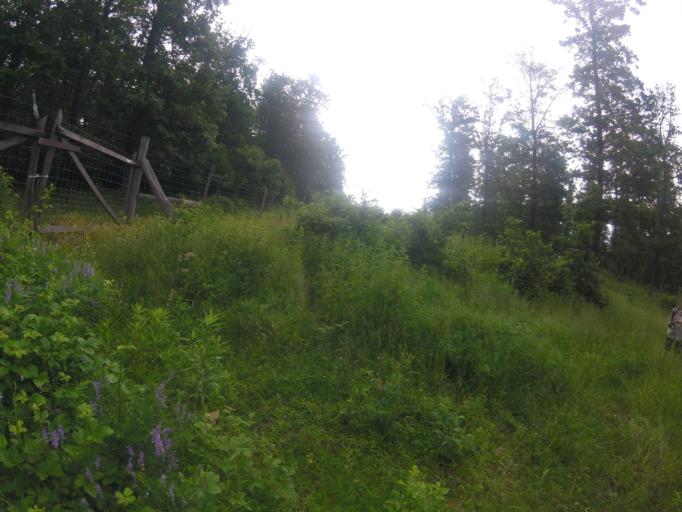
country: HU
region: Veszprem
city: Urkut
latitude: 47.0411
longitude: 17.6539
